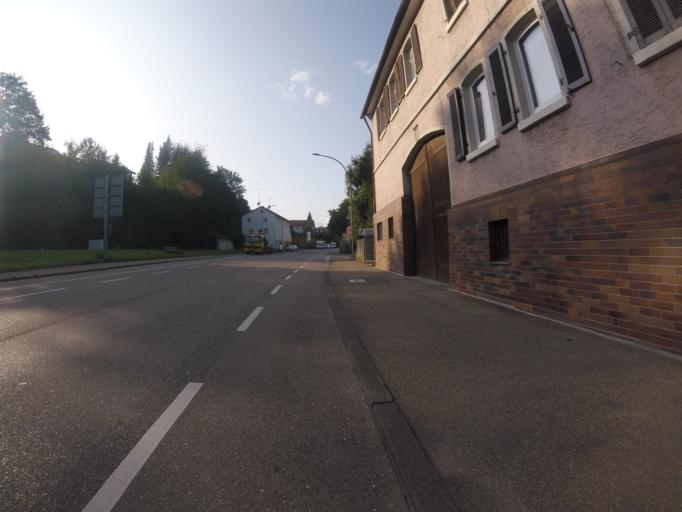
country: DE
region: Baden-Wuerttemberg
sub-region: Regierungsbezirk Stuttgart
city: Backnang
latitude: 48.9513
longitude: 9.4321
